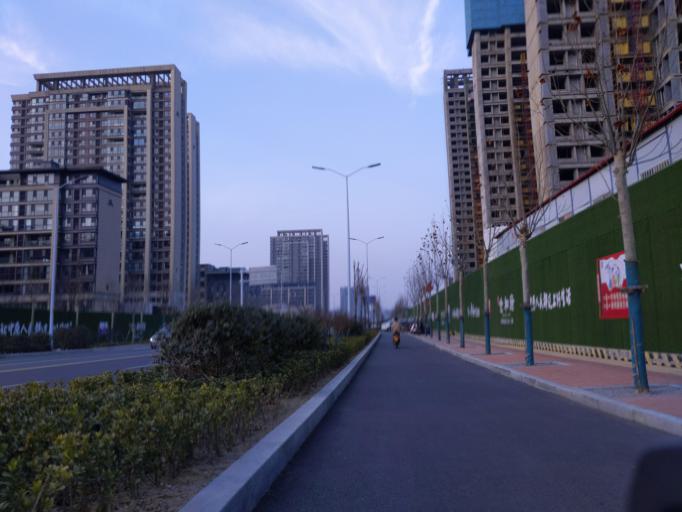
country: CN
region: Henan Sheng
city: Puyang
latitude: 35.8043
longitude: 115.0113
